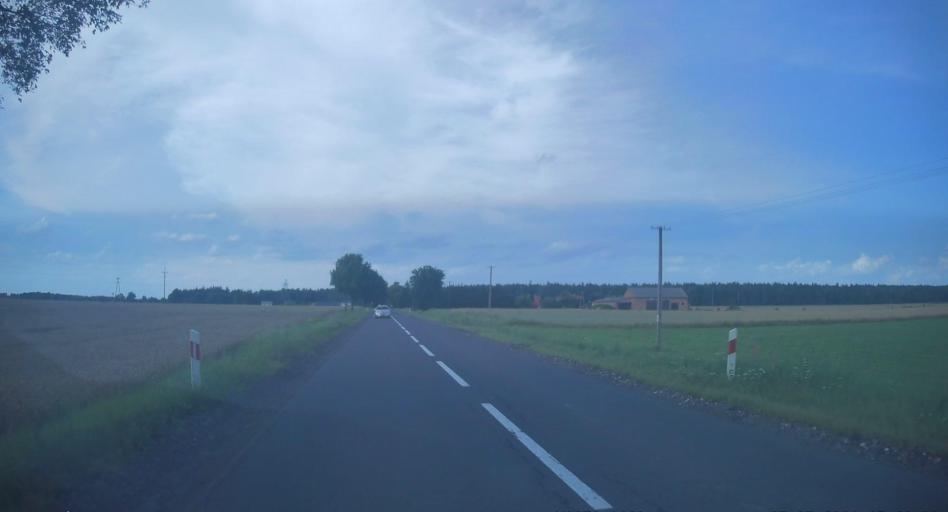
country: PL
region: Lodz Voivodeship
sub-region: Powiat tomaszowski
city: Rzeczyca
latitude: 51.6778
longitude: 20.2665
